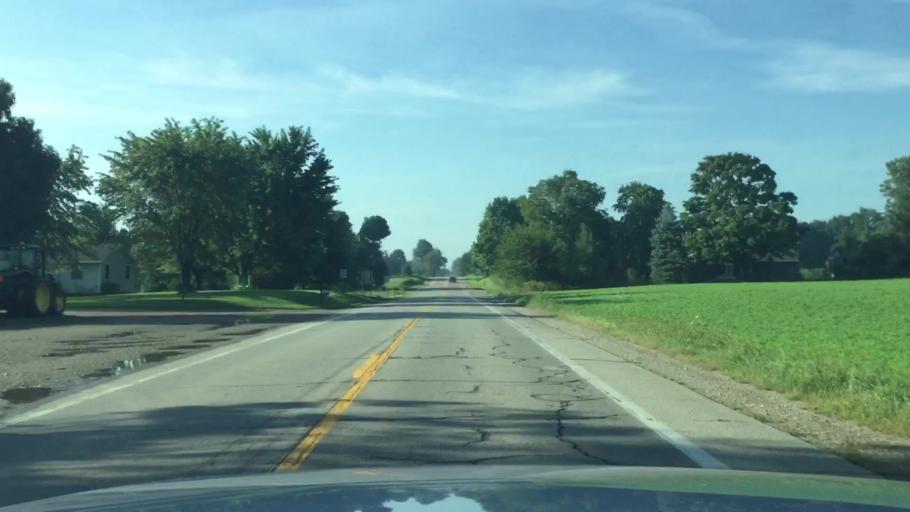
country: US
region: Michigan
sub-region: Lenawee County
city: Manitou Beach-Devils Lake
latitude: 41.9441
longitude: -84.3672
